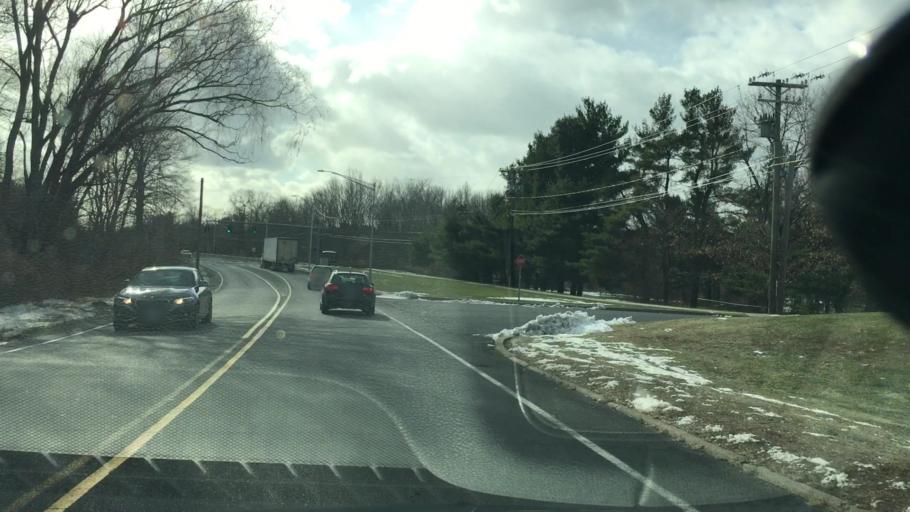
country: US
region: Connecticut
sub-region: New Haven County
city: Meriden
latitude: 41.5137
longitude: -72.7669
